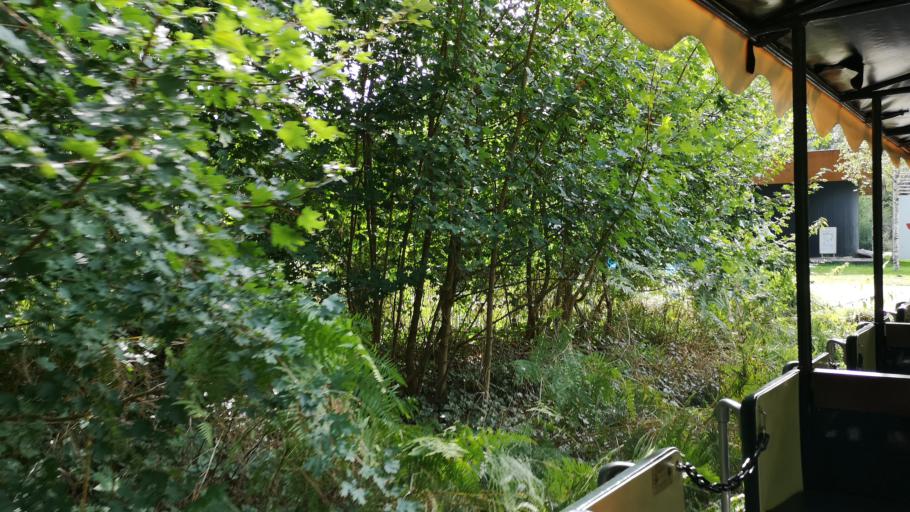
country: NL
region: North Holland
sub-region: Gemeente Ouder-Amstel
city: Ouderkerk aan de Amstel
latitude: 52.3289
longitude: 4.8924
